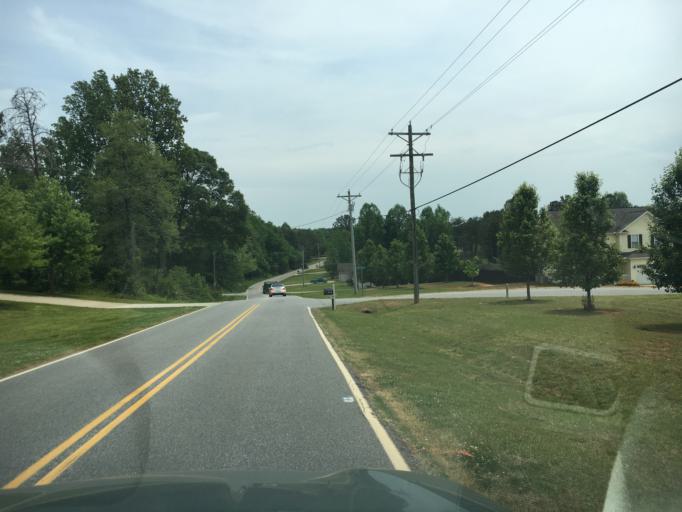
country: US
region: South Carolina
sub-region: Spartanburg County
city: Wellford
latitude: 34.9929
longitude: -82.1045
